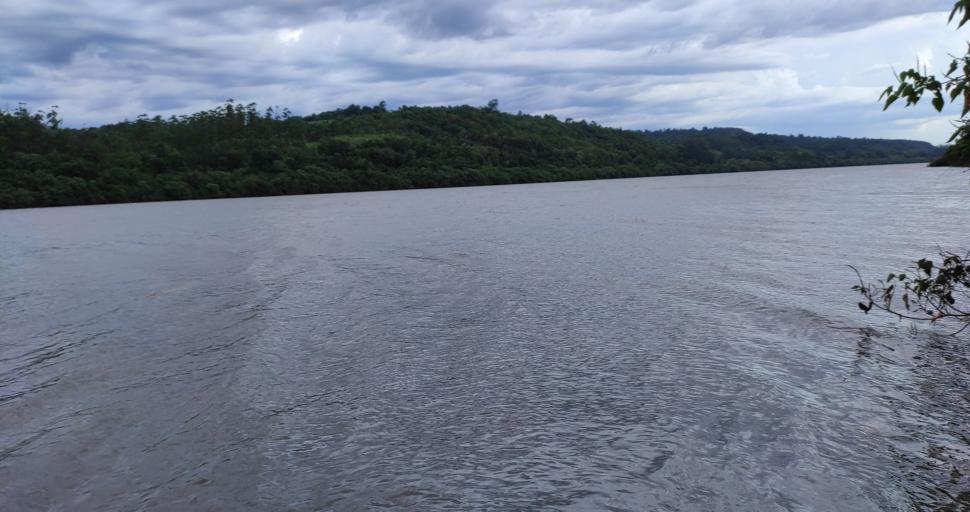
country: AR
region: Misiones
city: El Soberbio
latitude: -27.3047
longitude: -54.1932
